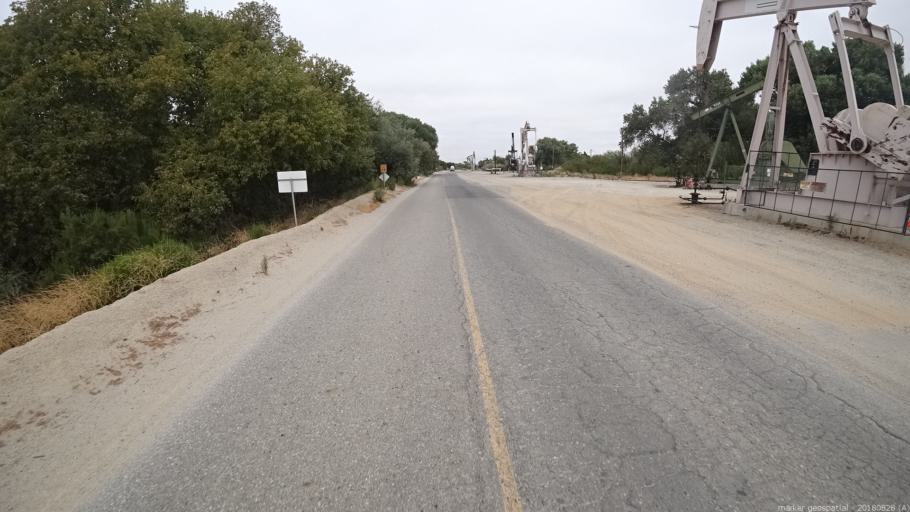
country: US
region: California
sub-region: San Luis Obispo County
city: Lake Nacimiento
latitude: 35.9578
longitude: -120.8775
